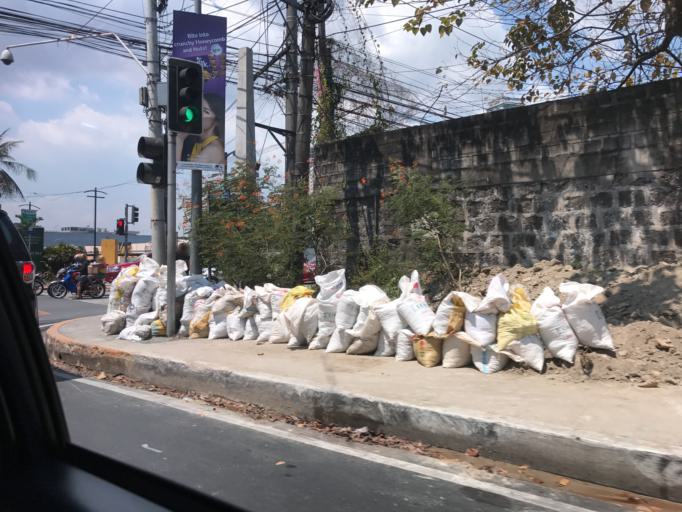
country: PH
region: Metro Manila
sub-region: San Juan
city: San Juan
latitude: 14.5995
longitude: 121.0499
